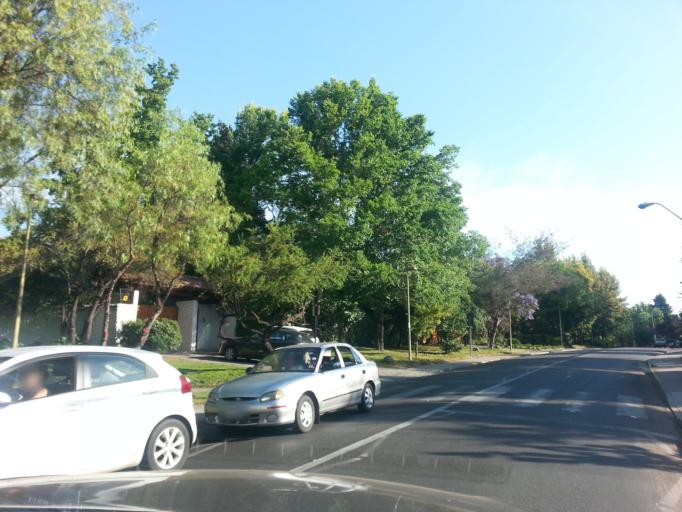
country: CL
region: Santiago Metropolitan
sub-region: Provincia de Santiago
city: Villa Presidente Frei, Nunoa, Santiago, Chile
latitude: -33.3944
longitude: -70.5310
